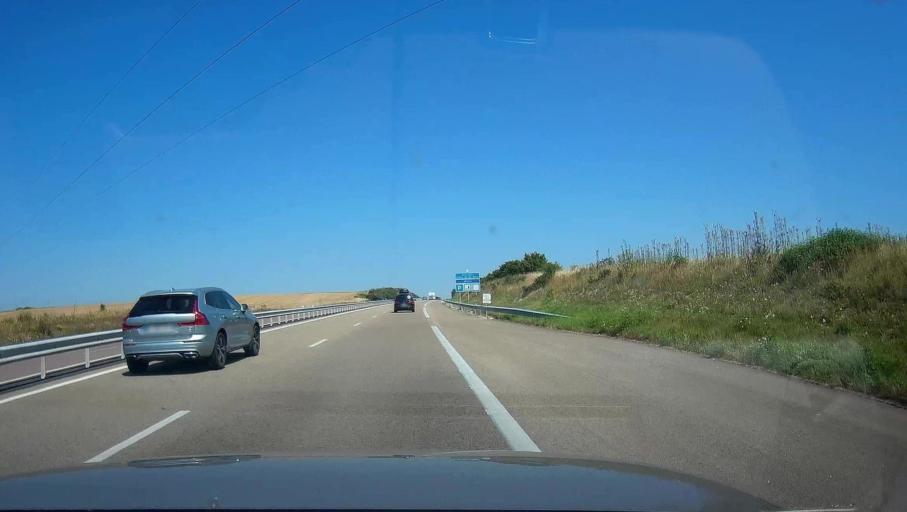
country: FR
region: Champagne-Ardenne
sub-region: Departement de l'Aube
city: Creney-pres-Troyes
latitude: 48.3177
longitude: 4.1643
